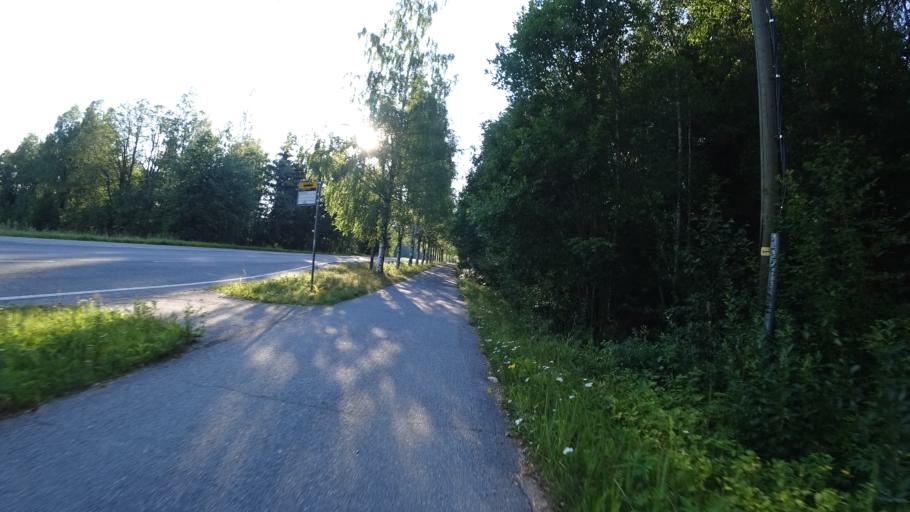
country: FI
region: Pirkanmaa
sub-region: Tampere
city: Nokia
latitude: 61.4709
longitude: 23.3877
